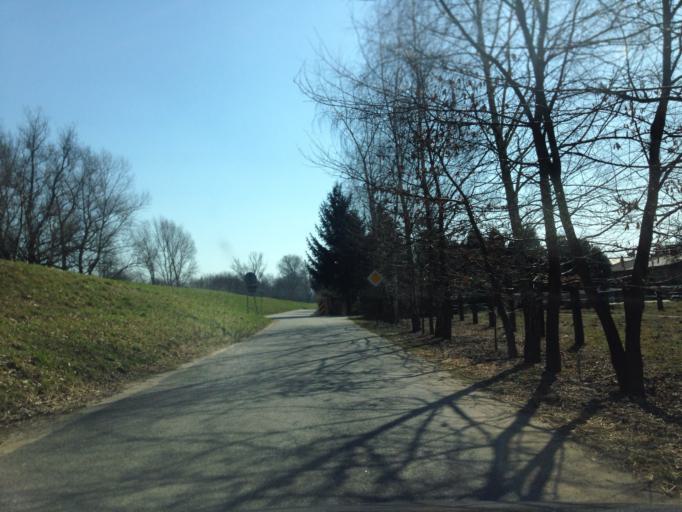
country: PL
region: Masovian Voivodeship
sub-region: Powiat piaseczynski
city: Konstancin-Jeziorna
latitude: 52.1297
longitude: 21.1695
